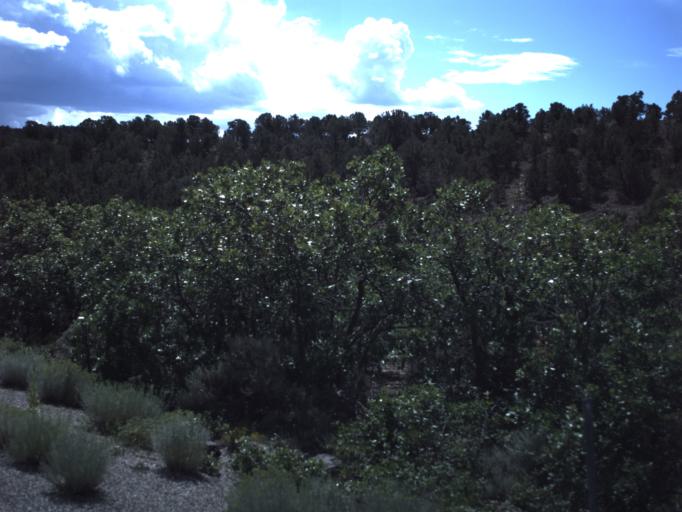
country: US
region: Utah
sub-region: Piute County
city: Junction
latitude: 38.2576
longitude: -112.2867
